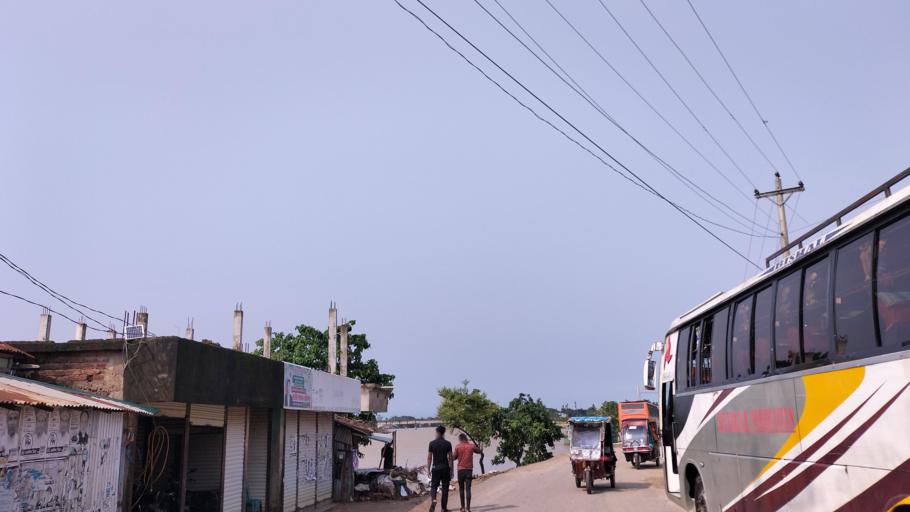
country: BD
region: Dhaka
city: Netrakona
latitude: 25.0712
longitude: 90.8863
